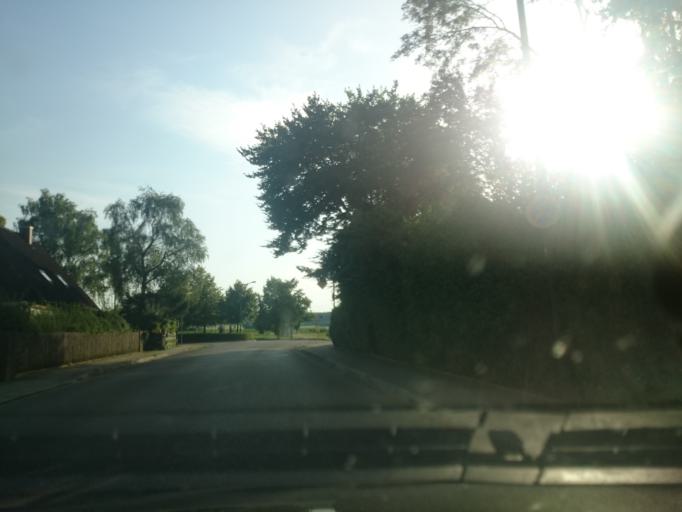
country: DE
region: Bavaria
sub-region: Upper Bavaria
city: Puchheim
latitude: 48.1289
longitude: 11.3481
